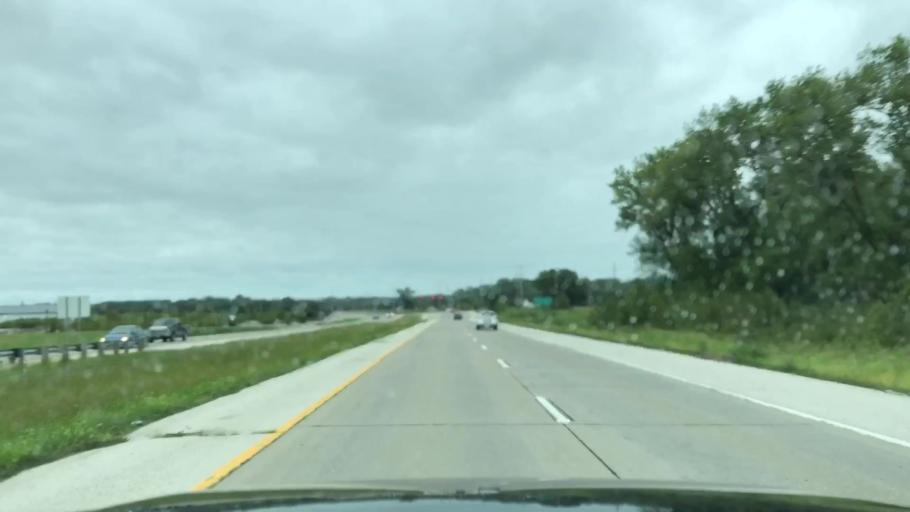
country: US
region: Missouri
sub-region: Saint Charles County
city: Saint Charles
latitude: 38.7293
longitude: -90.4912
